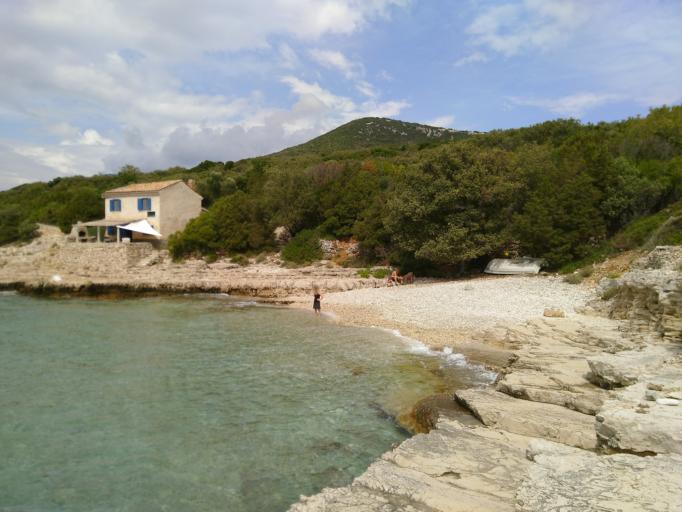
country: HR
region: Primorsko-Goranska
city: Mali Losinj
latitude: 44.6240
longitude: 14.3823
